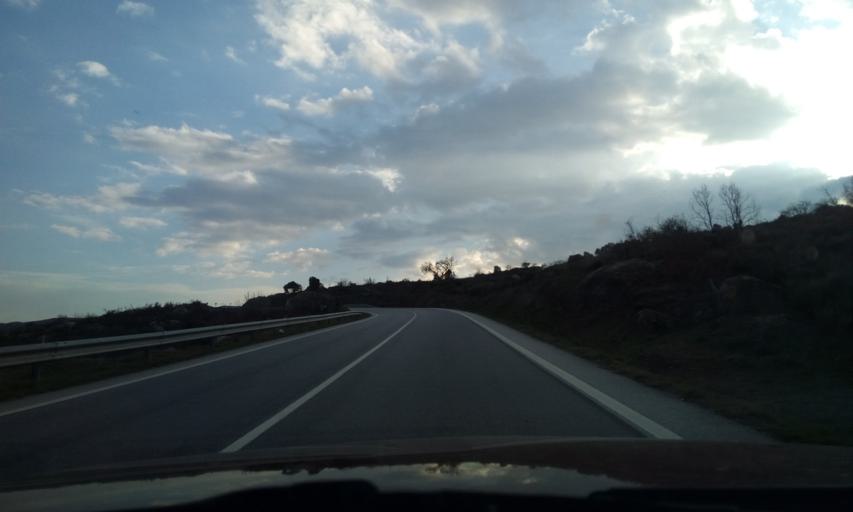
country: ES
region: Castille and Leon
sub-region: Provincia de Salamanca
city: Aldea del Obispo
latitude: 40.6973
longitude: -6.9341
